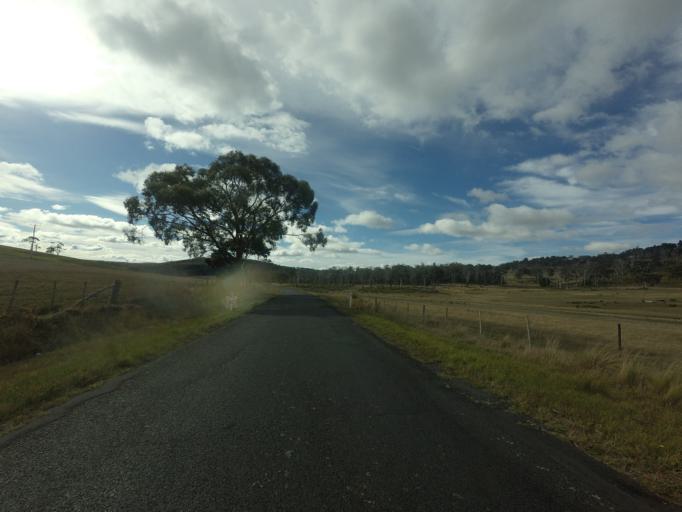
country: AU
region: Tasmania
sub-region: Brighton
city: Bridgewater
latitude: -42.3825
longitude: 147.3613
